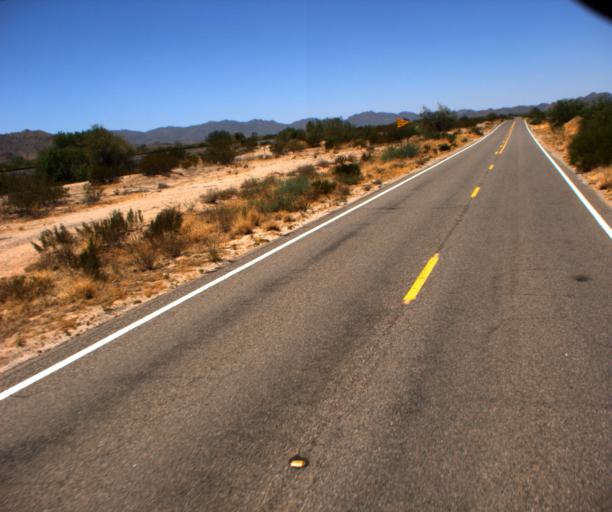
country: US
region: Arizona
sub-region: Pinal County
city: Maricopa
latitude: 33.0341
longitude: -112.3546
